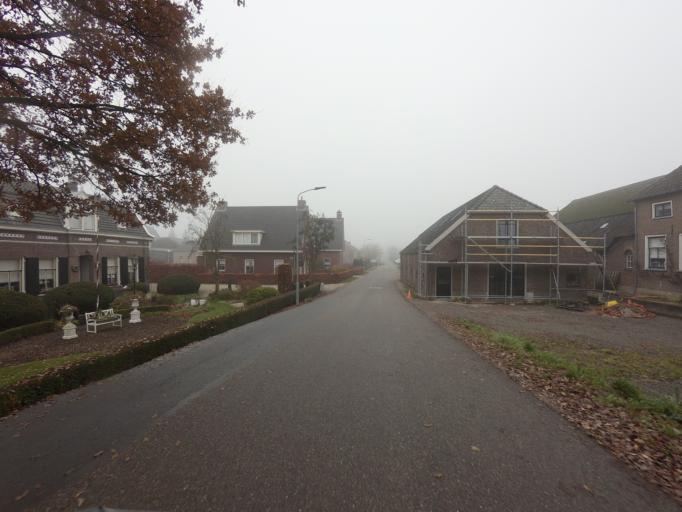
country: NL
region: Gelderland
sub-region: Gemeente Zaltbommel
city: Nederhemert
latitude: 51.7624
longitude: 5.1697
